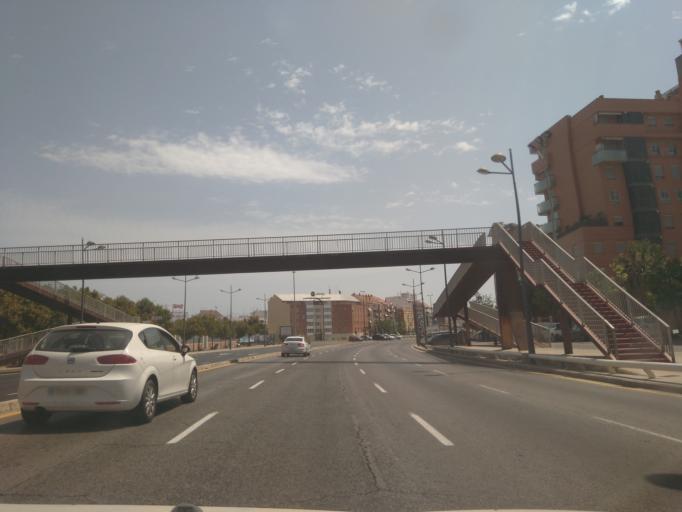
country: ES
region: Valencia
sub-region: Provincia de Valencia
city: Sedavi
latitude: 39.4478
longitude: -0.3695
